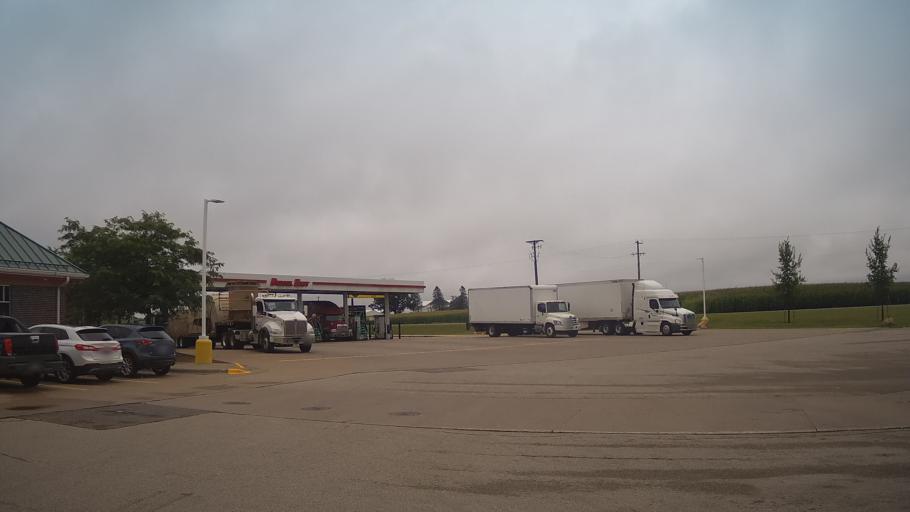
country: US
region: Wisconsin
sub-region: Trempealeau County
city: Trempealeau
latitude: 43.9240
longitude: -91.4400
